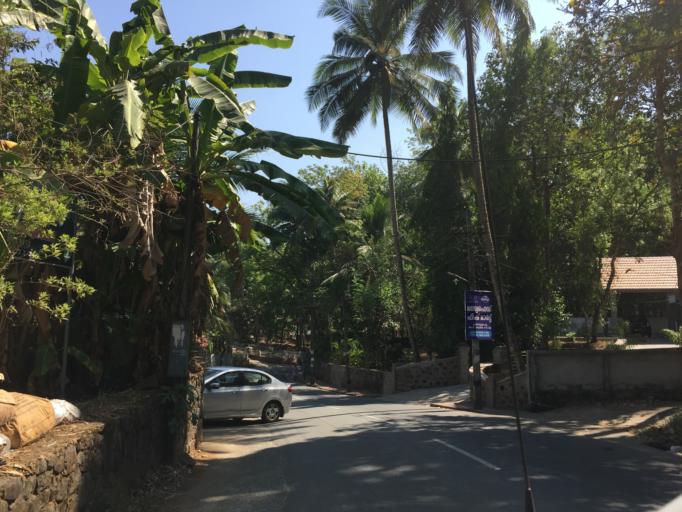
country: IN
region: Kerala
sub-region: Kottayam
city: Erattupetta
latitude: 9.6842
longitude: 76.7736
